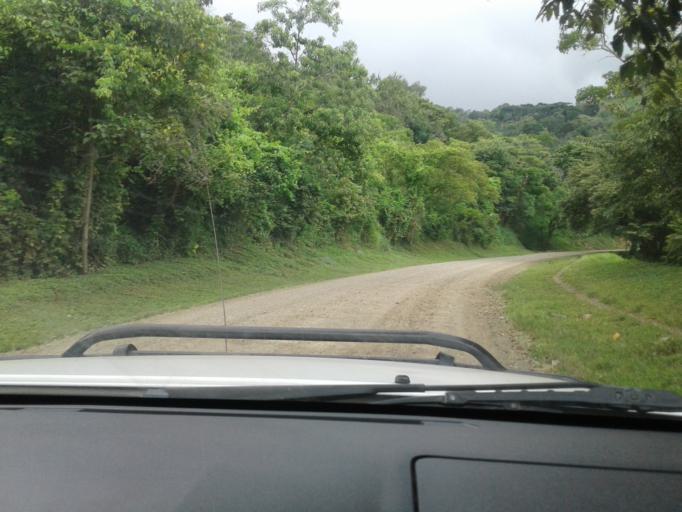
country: NI
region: Matagalpa
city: San Ramon
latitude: 12.9067
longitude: -85.8000
